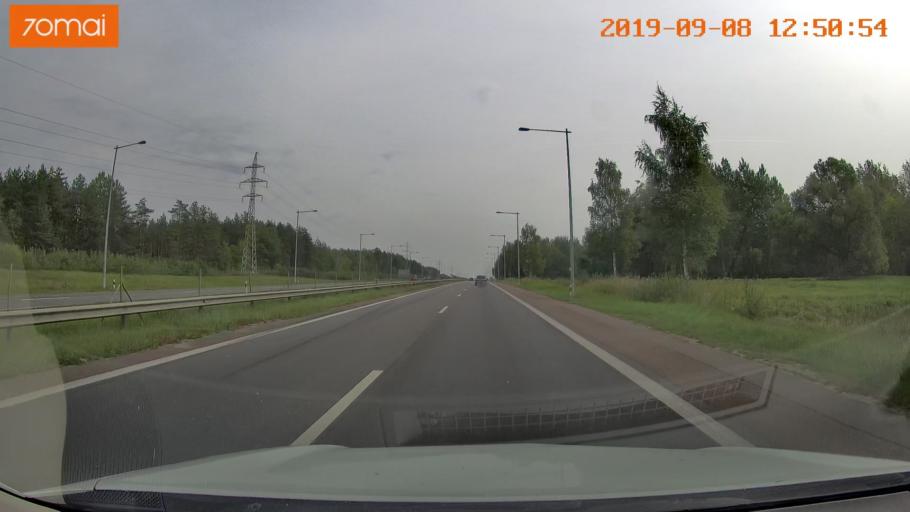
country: LT
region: Kauno apskritis
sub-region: Kaunas
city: Eiguliai
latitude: 54.9361
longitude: 23.9318
